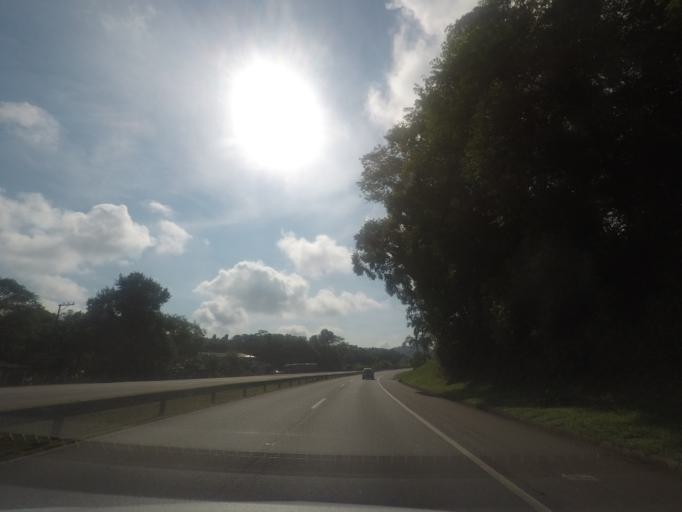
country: BR
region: Parana
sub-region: Antonina
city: Antonina
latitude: -25.5403
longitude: -48.7757
